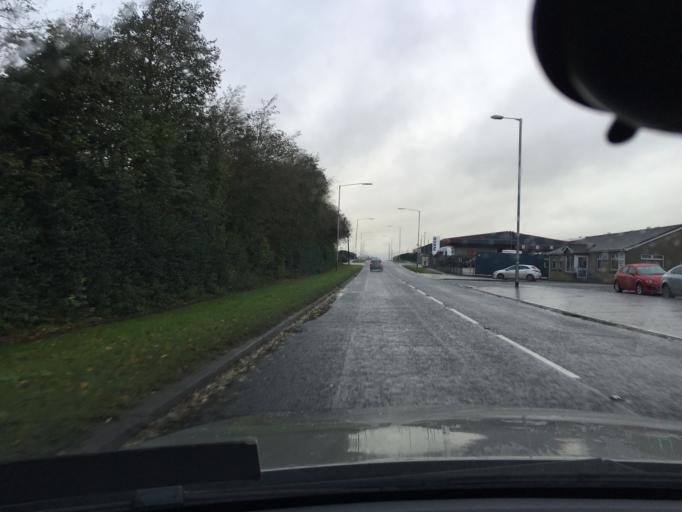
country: GB
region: Northern Ireland
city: Carnmoney
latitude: 54.6721
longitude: -5.9753
